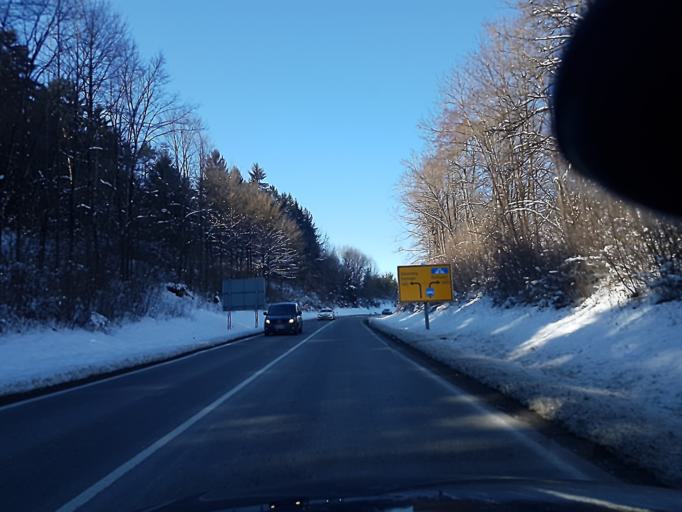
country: DE
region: Baden-Wuerttemberg
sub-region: Freiburg Region
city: Zimmern ob Rottweil
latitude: 48.1767
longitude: 8.5708
